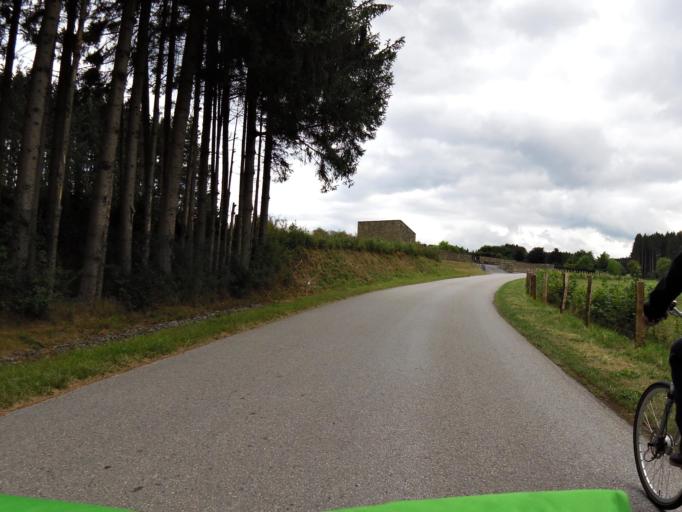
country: BE
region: Wallonia
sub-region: Province de Namur
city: Bievre
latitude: 49.9362
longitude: 5.0182
